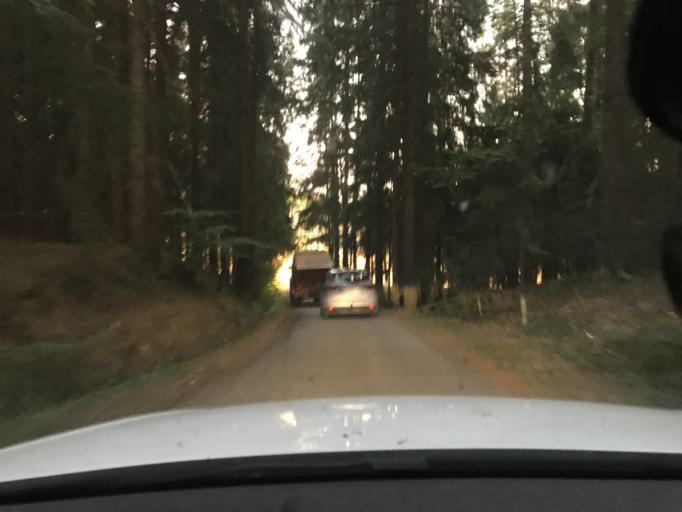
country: DE
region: Bavaria
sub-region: Upper Palatinate
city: Auerbach
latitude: 49.7428
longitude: 11.6172
